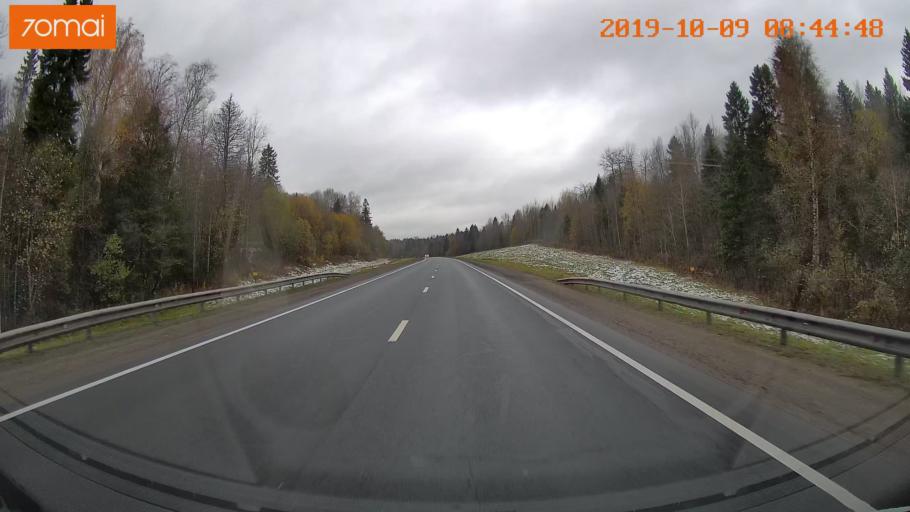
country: RU
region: Vologda
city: Gryazovets
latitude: 59.0411
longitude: 40.1036
